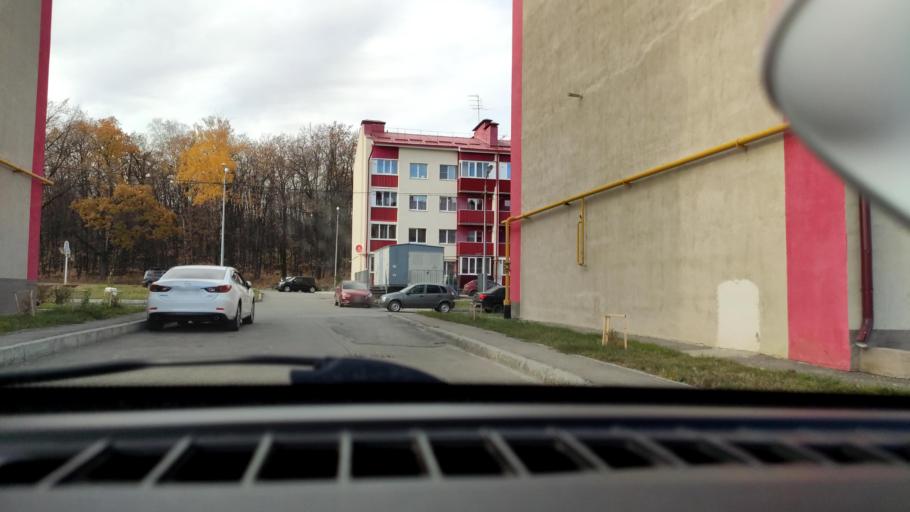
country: RU
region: Samara
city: Novosemeykino
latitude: 53.3314
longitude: 50.3150
